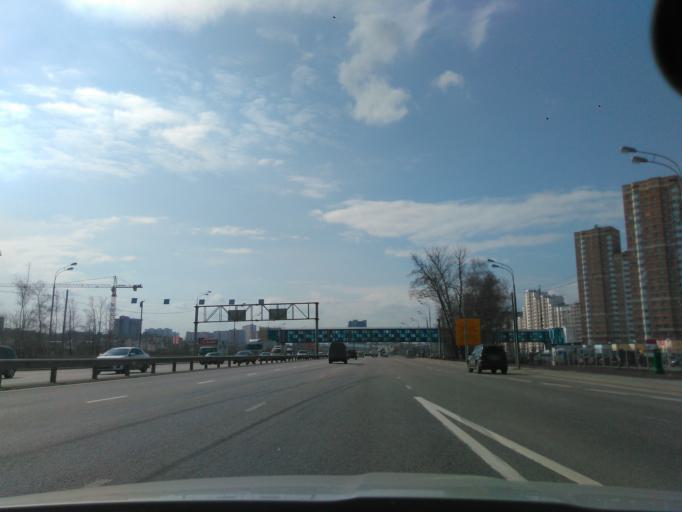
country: RU
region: Moscow
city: Severnyy
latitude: 55.9277
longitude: 37.5469
